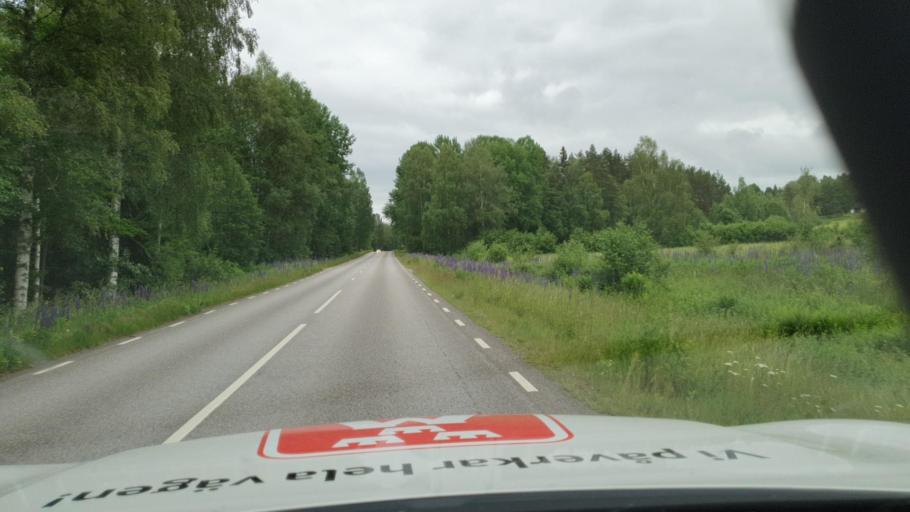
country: SE
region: Vaermland
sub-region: Sunne Kommun
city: Sunne
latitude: 59.8029
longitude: 13.0462
